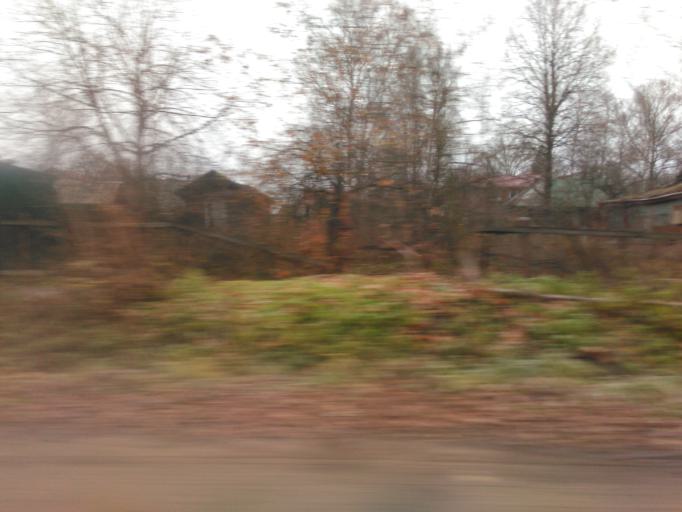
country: RU
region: Moskovskaya
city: Ashukino
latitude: 56.1655
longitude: 37.9472
